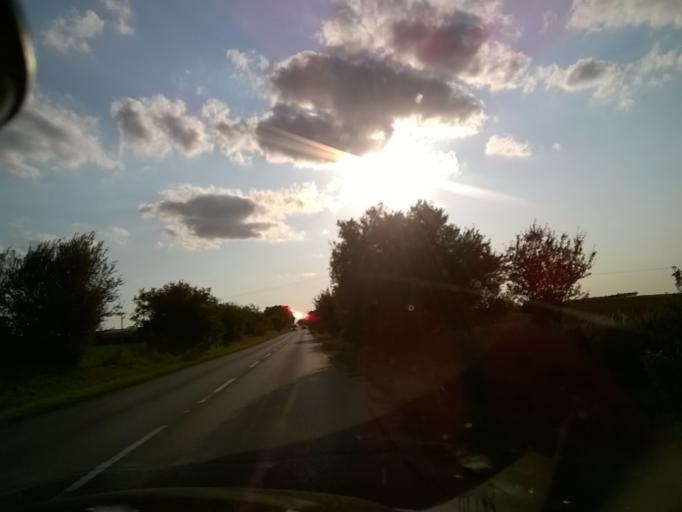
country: SK
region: Nitriansky
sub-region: Okres Nitra
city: Nitra
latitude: 48.3101
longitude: 17.9557
